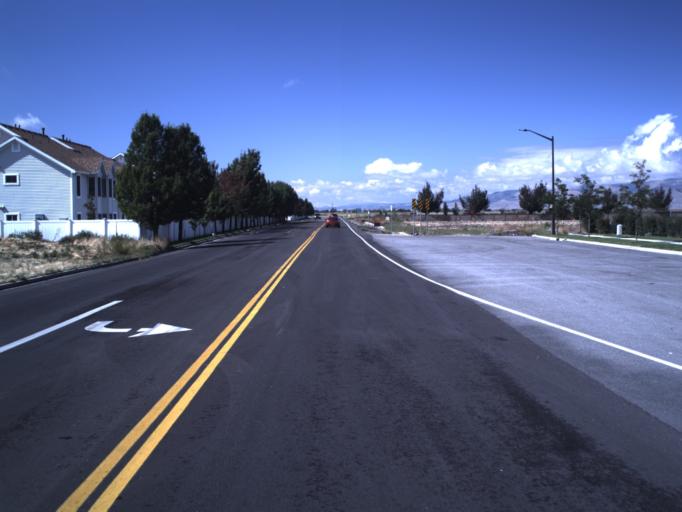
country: US
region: Utah
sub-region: Utah County
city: Springville
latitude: 40.1613
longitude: -111.6514
